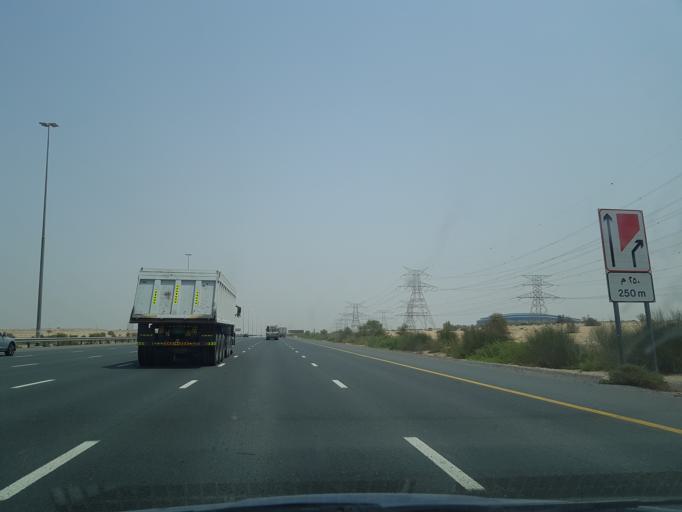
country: AE
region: Dubai
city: Dubai
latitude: 25.0473
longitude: 55.3072
